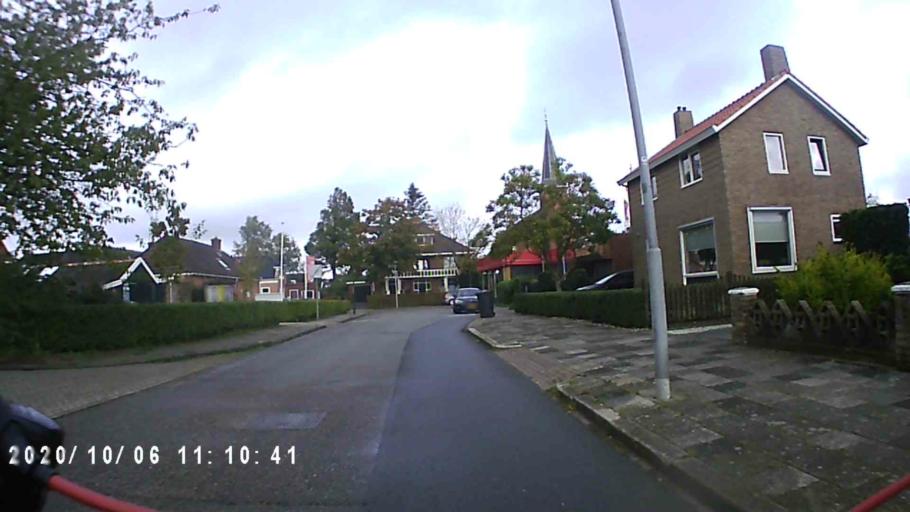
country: NL
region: Groningen
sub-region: Gemeente De Marne
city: Ulrum
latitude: 53.3601
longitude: 6.3800
